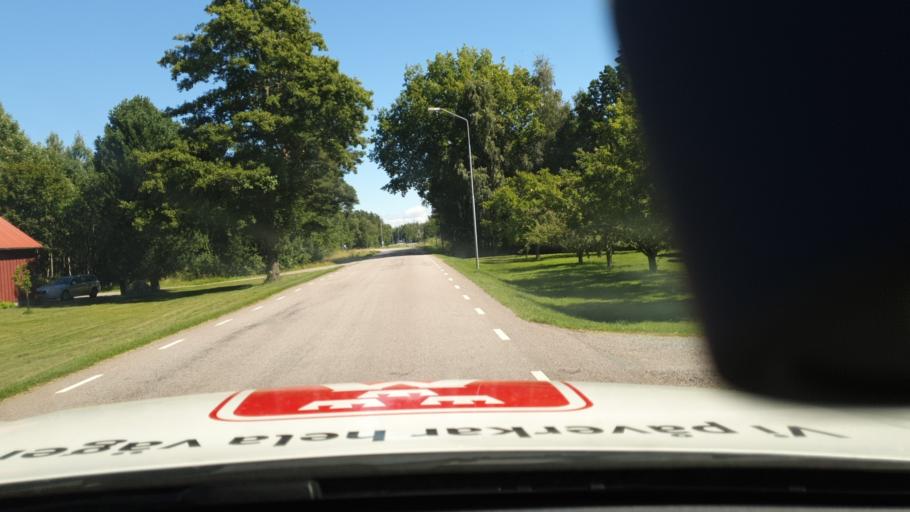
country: SE
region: Vaestra Goetaland
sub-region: Lidkopings Kommun
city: Vinninga
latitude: 58.4469
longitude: 13.2389
